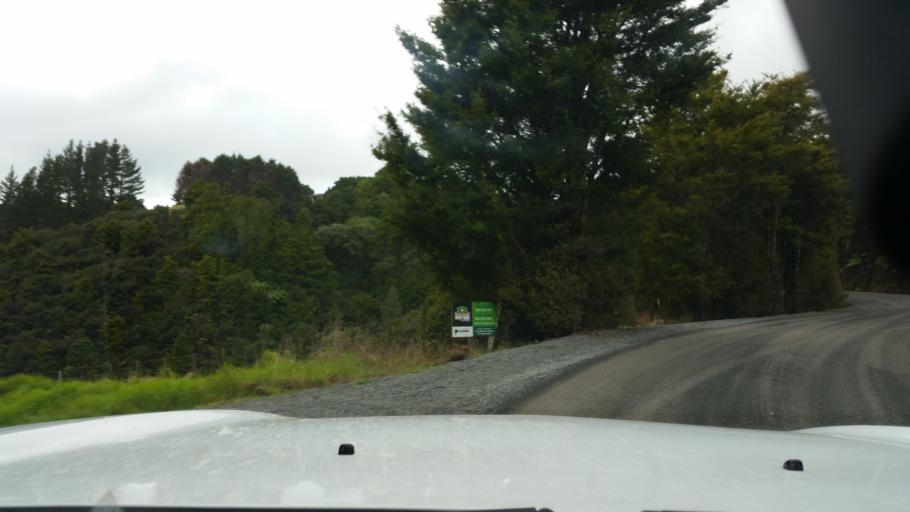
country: NZ
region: Northland
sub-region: Whangarei
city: Whangarei
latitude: -35.7338
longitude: 174.4338
